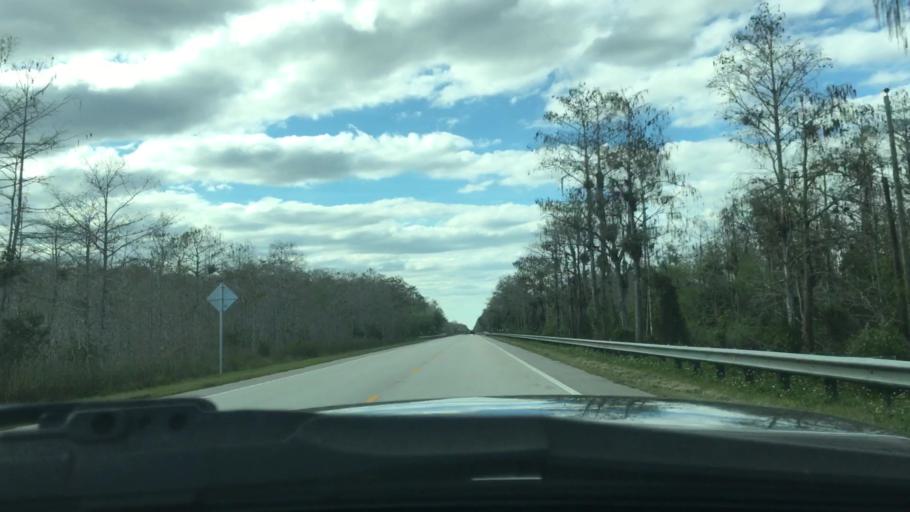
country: US
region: Florida
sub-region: Miami-Dade County
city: Kendall West
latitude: 25.8489
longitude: -80.9563
